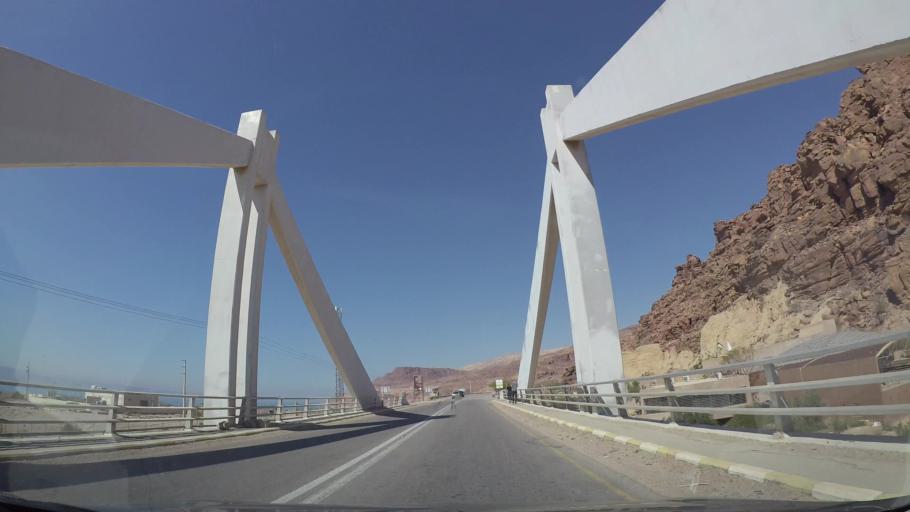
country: JO
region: Karak
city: Al Qasr
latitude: 31.4668
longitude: 35.5727
